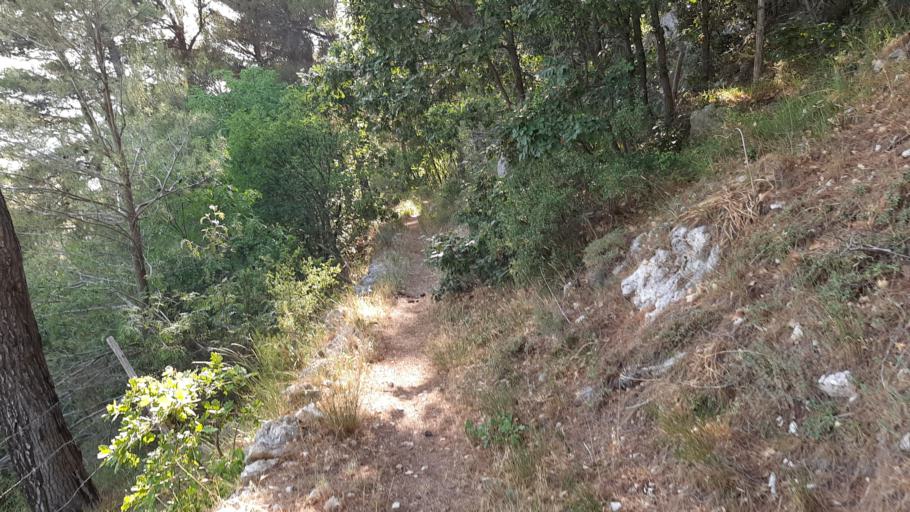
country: IT
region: Apulia
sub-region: Provincia di Foggia
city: San Giovanni Rotondo
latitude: 41.7106
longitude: 15.7152
